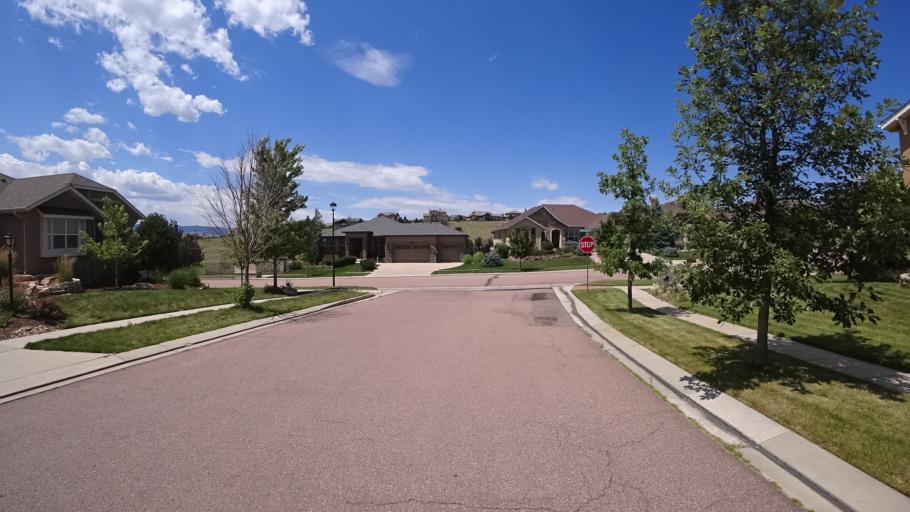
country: US
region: Colorado
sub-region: El Paso County
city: Black Forest
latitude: 38.9711
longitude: -104.7617
